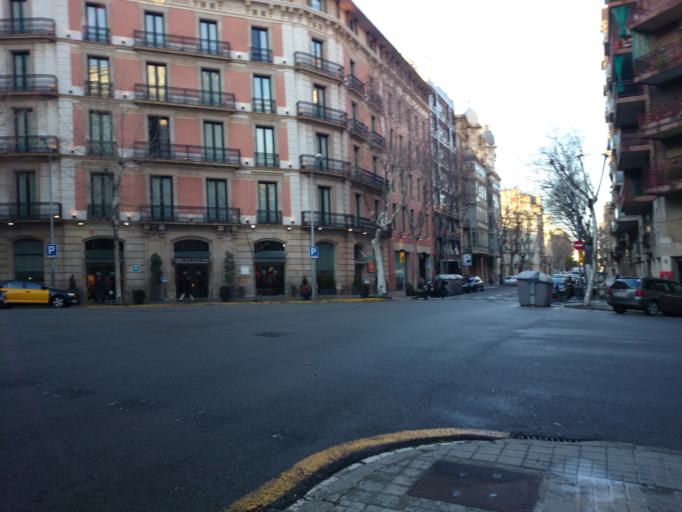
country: ES
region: Catalonia
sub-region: Provincia de Barcelona
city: Ciutat Vella
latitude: 41.3912
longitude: 2.1781
